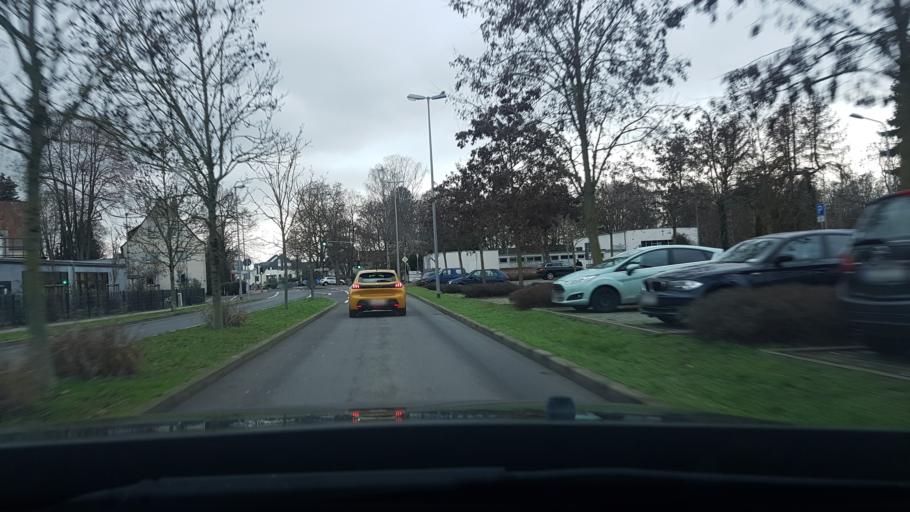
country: DE
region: Hesse
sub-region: Regierungsbezirk Darmstadt
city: Kriftel
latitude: 50.0884
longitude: 8.4761
